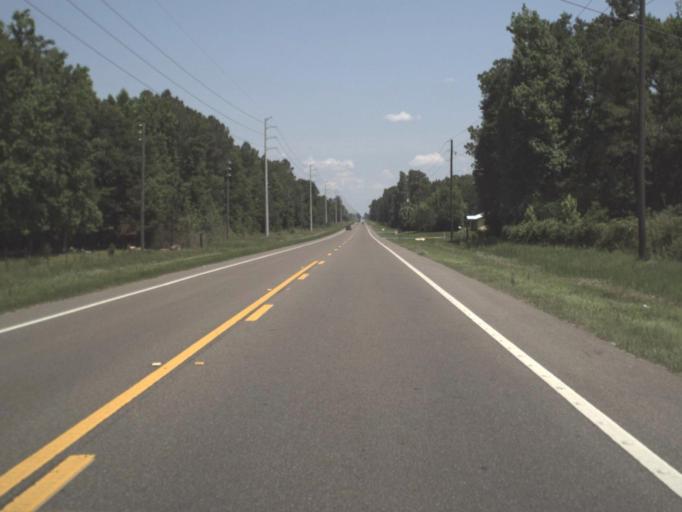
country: US
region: Florida
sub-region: Clay County
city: Keystone Heights
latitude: 29.8454
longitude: -82.0674
